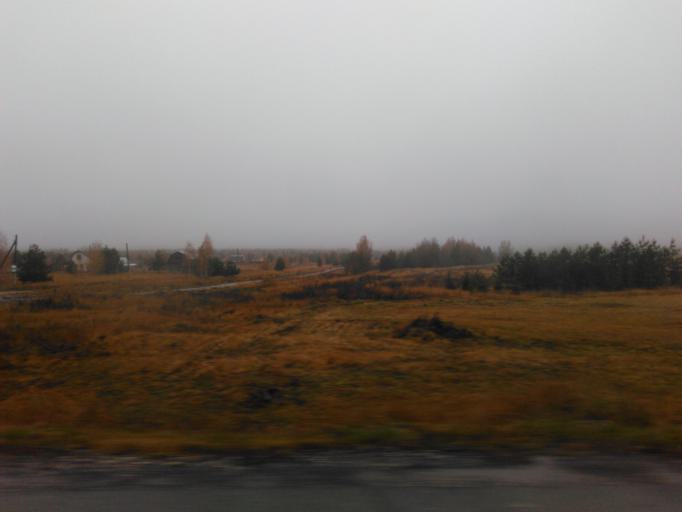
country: RU
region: Tatarstan
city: Sviyazhsk
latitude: 55.7335
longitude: 48.7764
